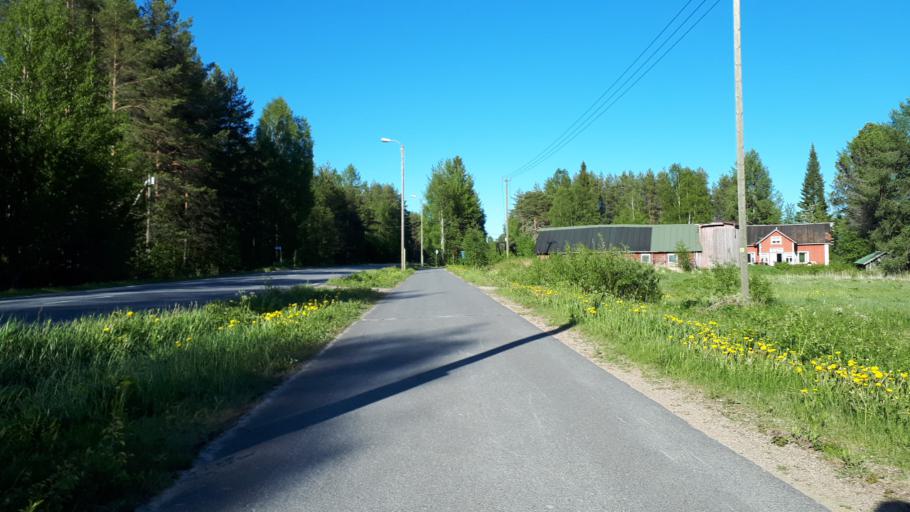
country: FI
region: Northern Ostrobothnia
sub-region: Oulunkaari
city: Ii
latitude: 65.3244
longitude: 25.4933
